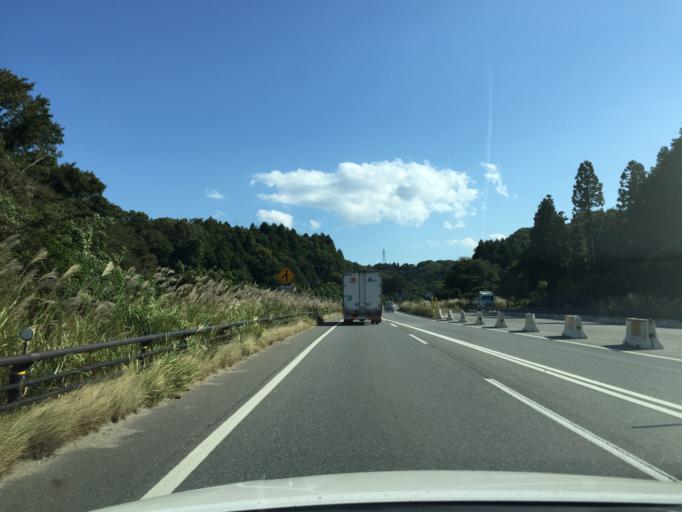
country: JP
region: Fukushima
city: Iwaki
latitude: 37.0425
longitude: 140.8750
